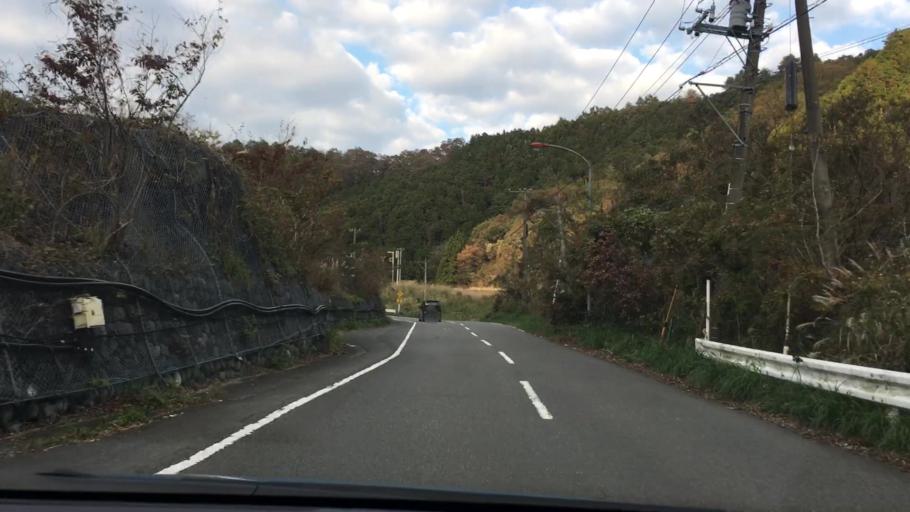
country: JP
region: Yamanashi
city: Uenohara
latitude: 35.5561
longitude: 139.1388
